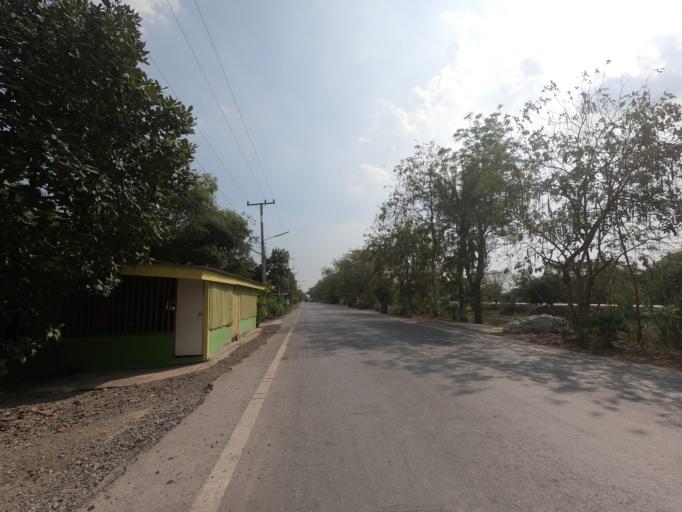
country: TH
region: Pathum Thani
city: Nong Suea
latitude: 14.1085
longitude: 100.8466
